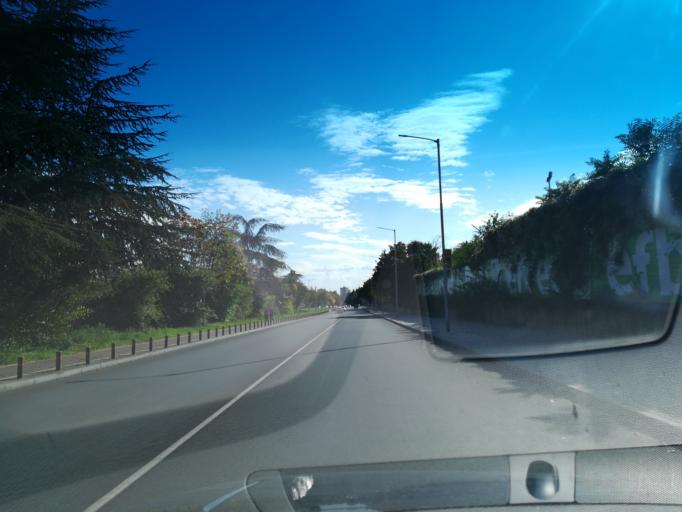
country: BG
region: Stara Zagora
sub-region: Obshtina Stara Zagora
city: Stara Zagora
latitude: 42.4416
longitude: 25.6349
